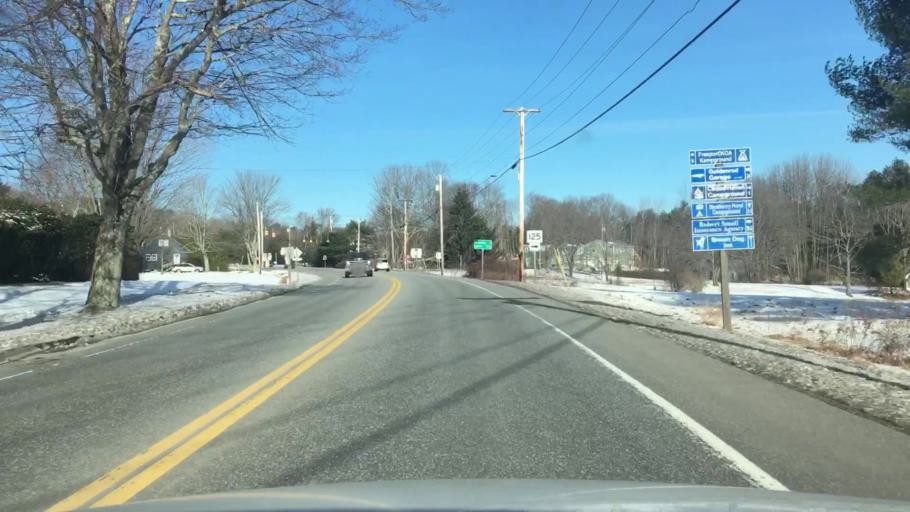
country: US
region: Maine
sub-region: Cumberland County
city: Freeport
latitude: 43.8741
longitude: -70.1068
